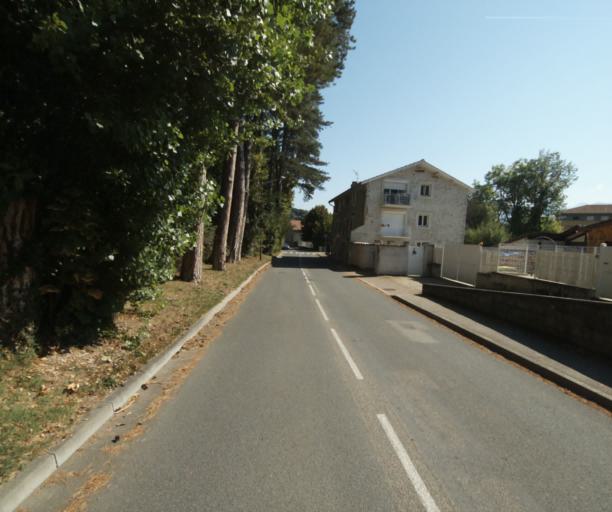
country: FR
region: Rhone-Alpes
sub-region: Departement de l'Isere
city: Allieres-et-Risset
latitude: 45.0915
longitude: 5.6786
